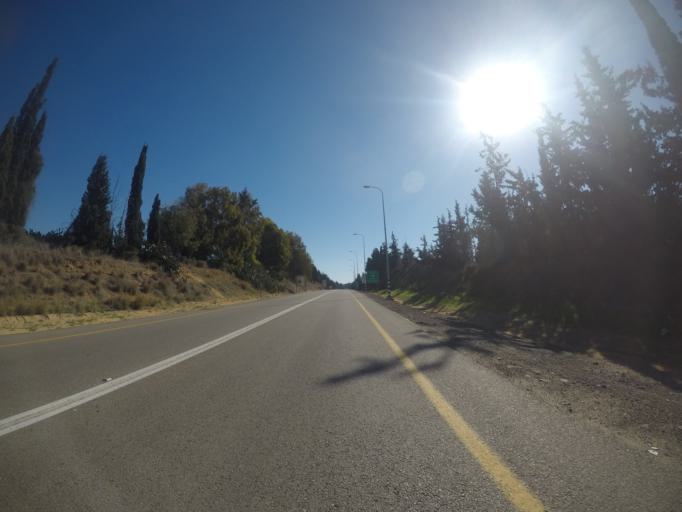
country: IL
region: Southern District
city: Ashdod
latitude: 31.7237
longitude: 34.6368
